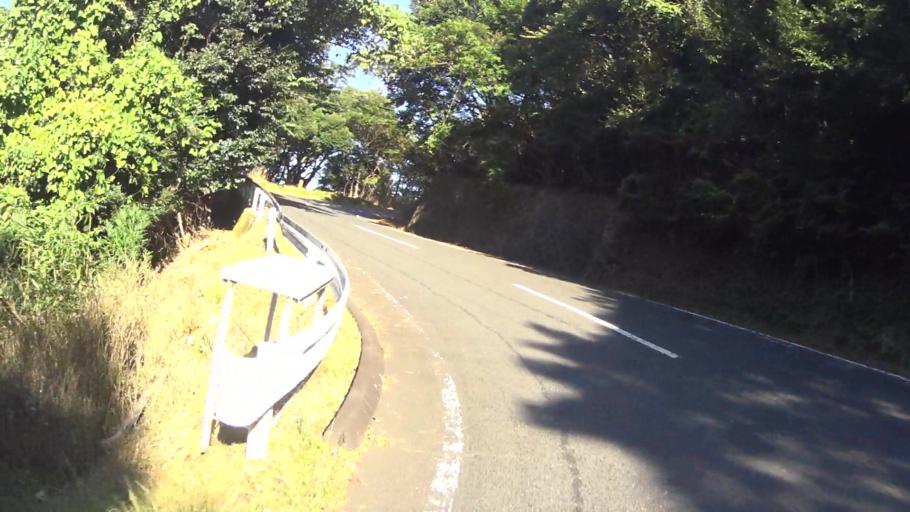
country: JP
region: Hyogo
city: Toyooka
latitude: 35.6465
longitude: 134.8826
